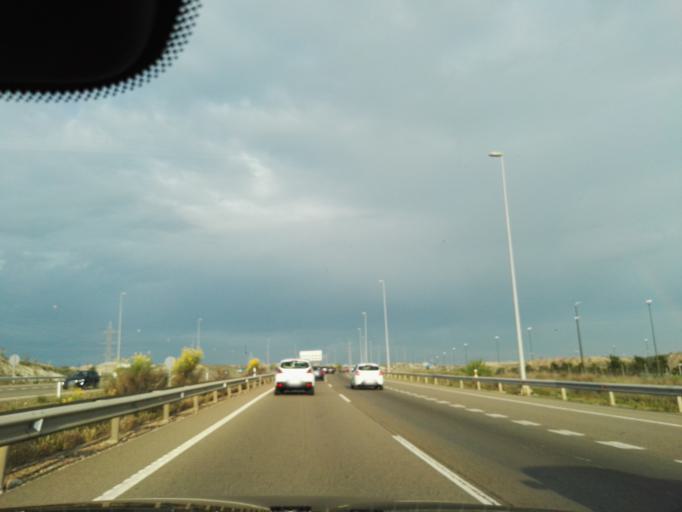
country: ES
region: Aragon
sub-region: Provincia de Zaragoza
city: Cuarte de Huerva
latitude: 41.6052
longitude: -0.8889
